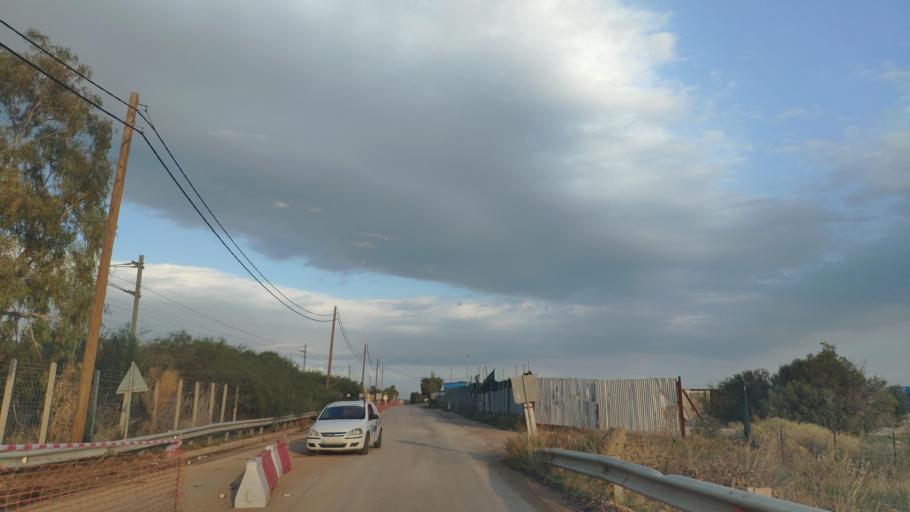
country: GR
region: Attica
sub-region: Nomarchia Dytikis Attikis
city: Nea Peramos
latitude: 38.0082
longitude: 23.4018
